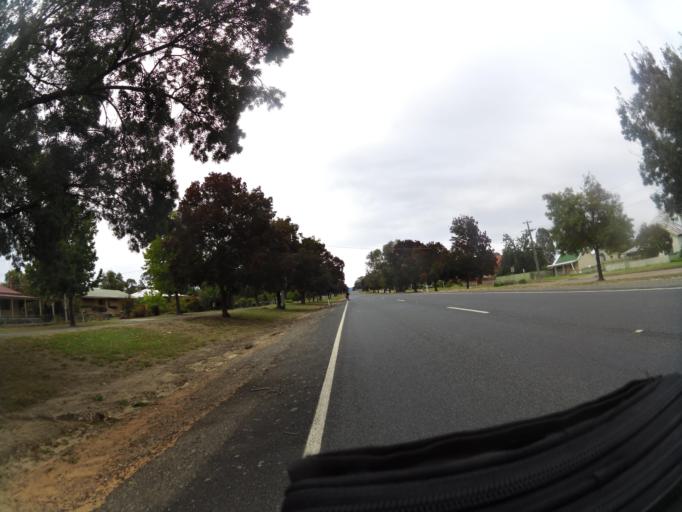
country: AU
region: New South Wales
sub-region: Snowy River
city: Jindabyne
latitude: -36.1880
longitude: 147.9160
